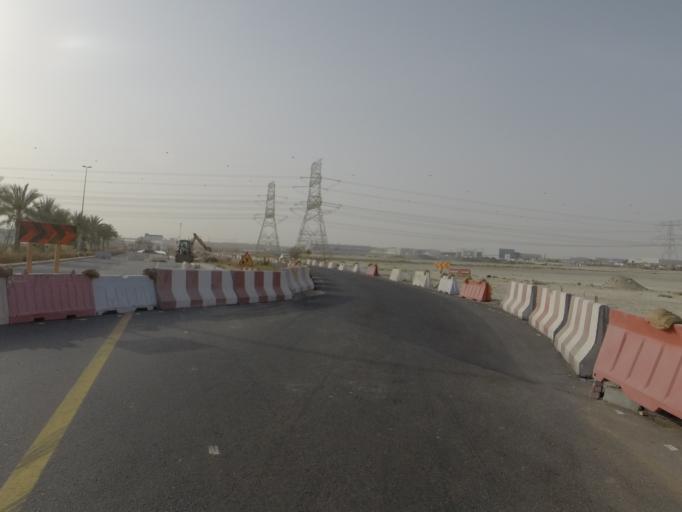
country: AE
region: Dubai
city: Dubai
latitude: 24.9565
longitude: 55.1031
